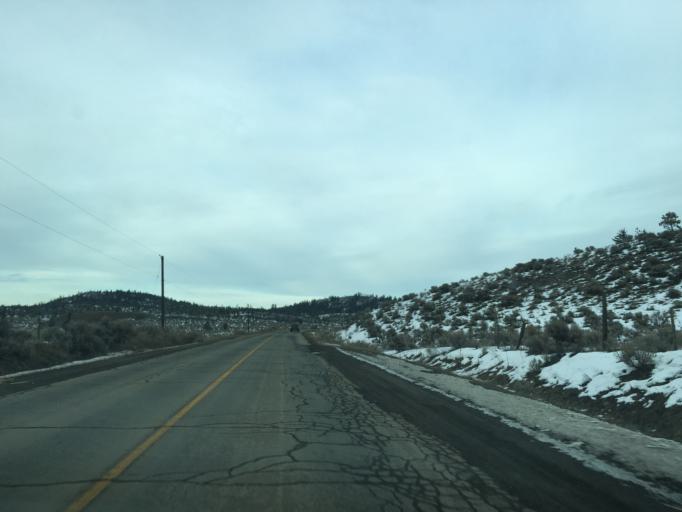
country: CA
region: British Columbia
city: Kamloops
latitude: 50.6245
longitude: -120.4434
